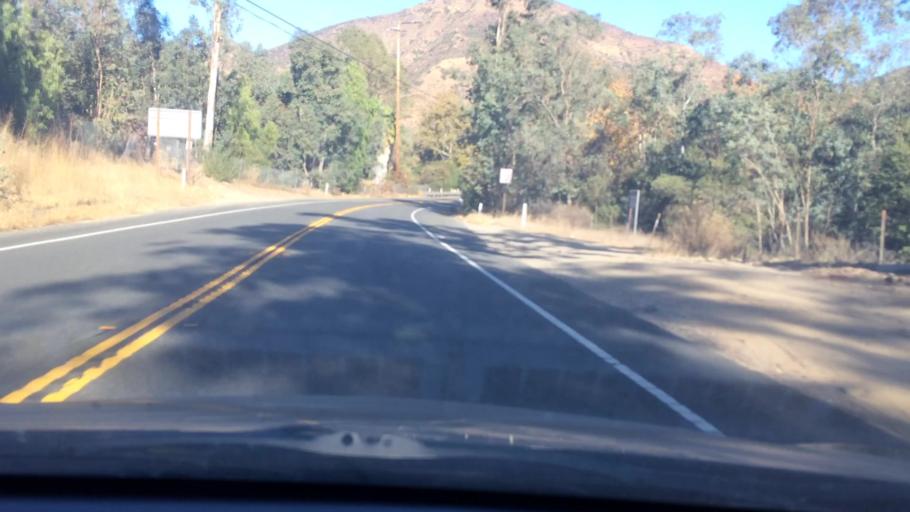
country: US
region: California
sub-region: Orange County
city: Coto De Caza
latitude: 33.5884
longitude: -117.5169
